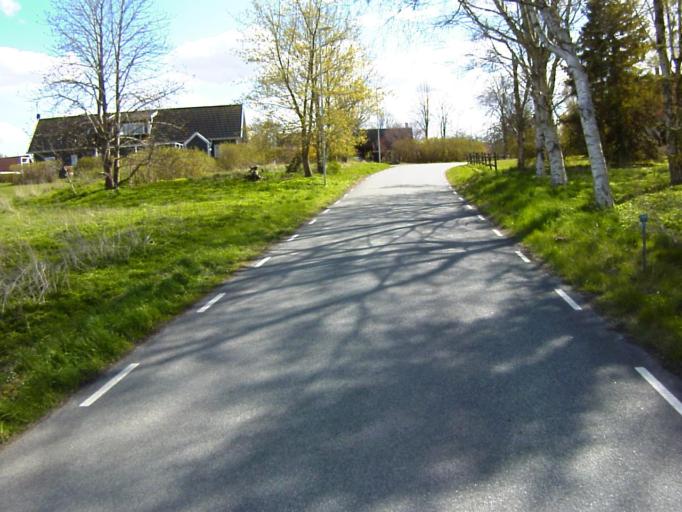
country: SE
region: Skane
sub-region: Kristianstads Kommun
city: Kristianstad
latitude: 56.0121
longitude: 14.0909
